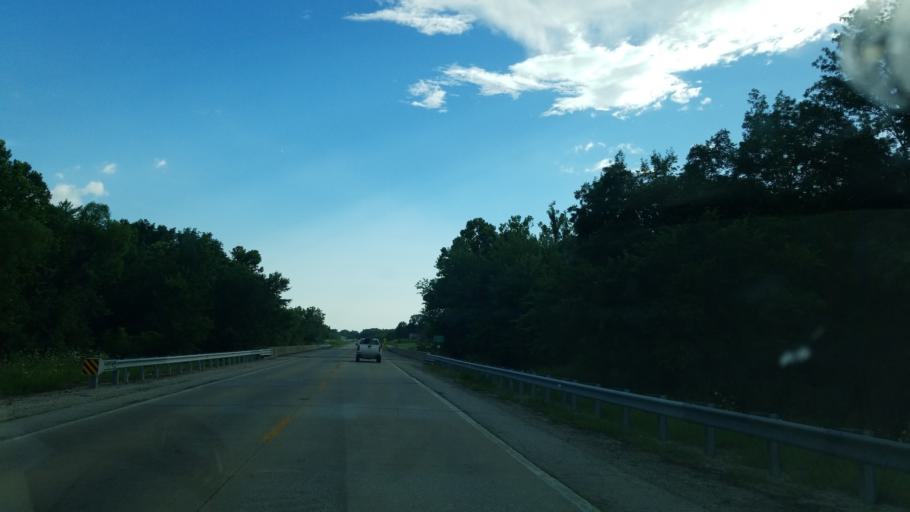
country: US
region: Illinois
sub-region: Marion County
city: Central City
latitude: 38.5638
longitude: -89.1184
